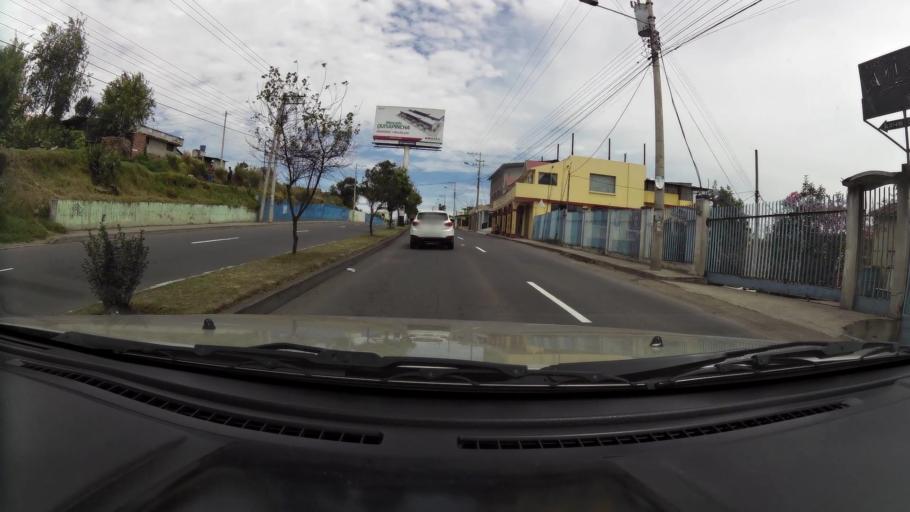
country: EC
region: Cotopaxi
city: San Miguel de Salcedo
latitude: -1.1018
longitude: -78.5913
